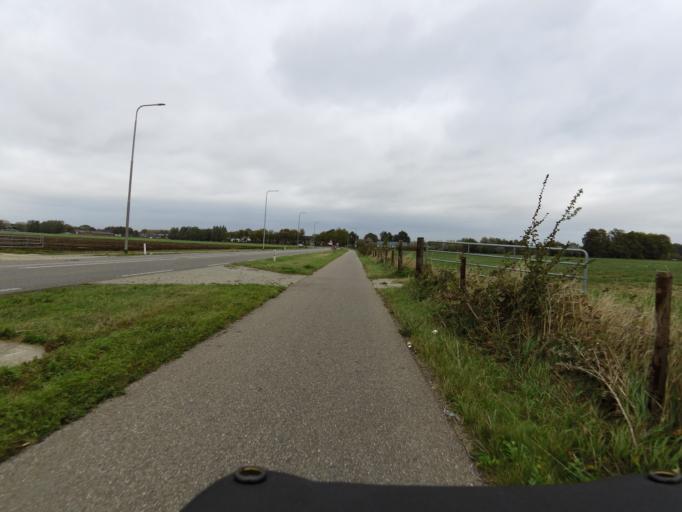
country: NL
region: Gelderland
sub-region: Gemeente Zevenaar
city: Zevenaar
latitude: 51.9016
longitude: 6.1096
